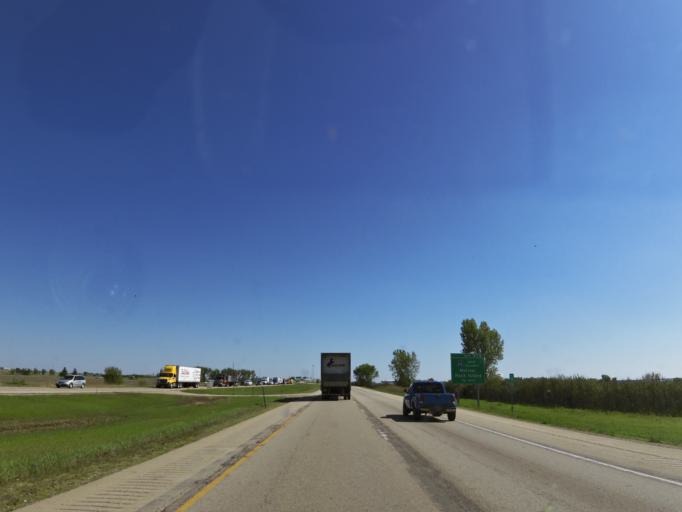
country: US
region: Illinois
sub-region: Ogle County
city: Rochelle
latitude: 41.9182
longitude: -89.0242
